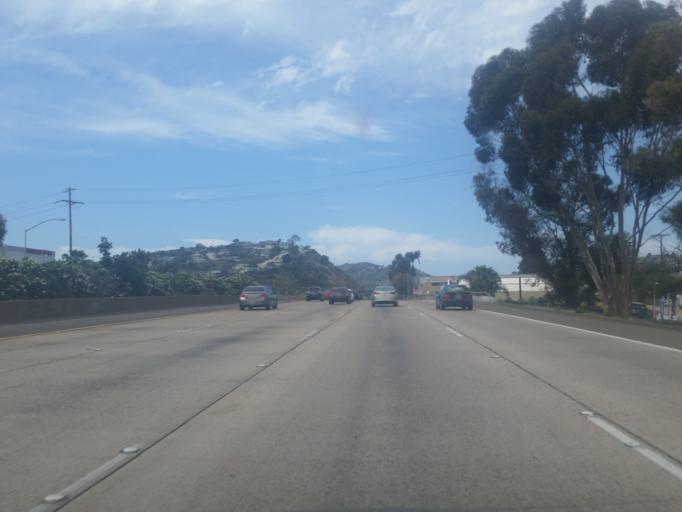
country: US
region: California
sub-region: San Diego County
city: La Jolla
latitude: 32.8060
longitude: -117.2150
